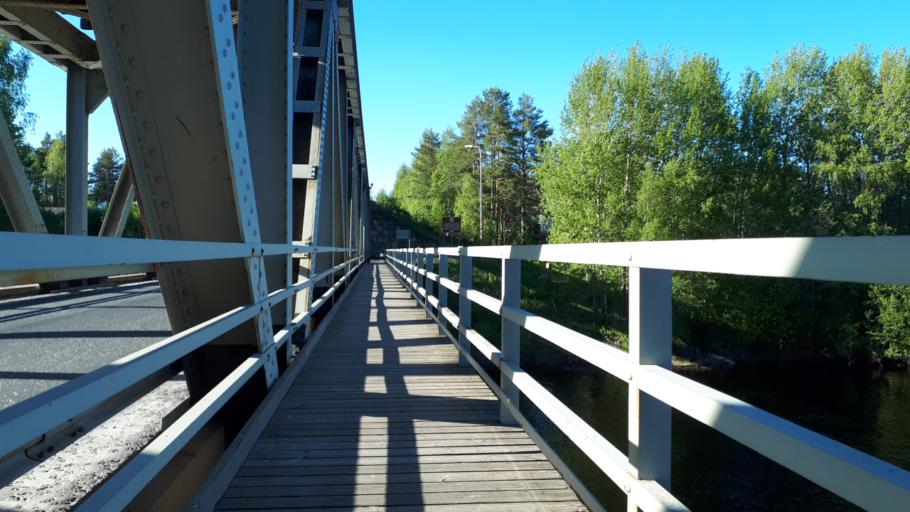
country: FI
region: Northern Ostrobothnia
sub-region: Oulunkaari
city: Ii
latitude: 65.3216
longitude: 25.4423
